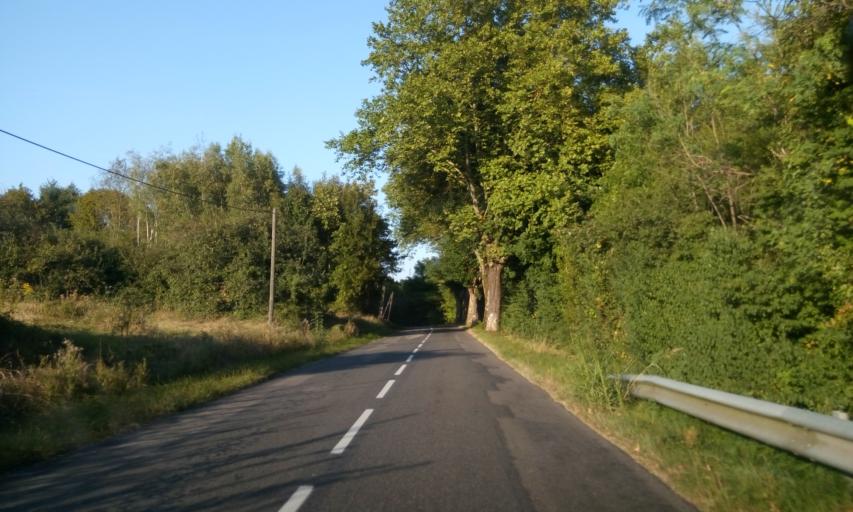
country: FR
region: Rhone-Alpes
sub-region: Departement de l'Ain
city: Priay
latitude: 46.0299
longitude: 5.3068
